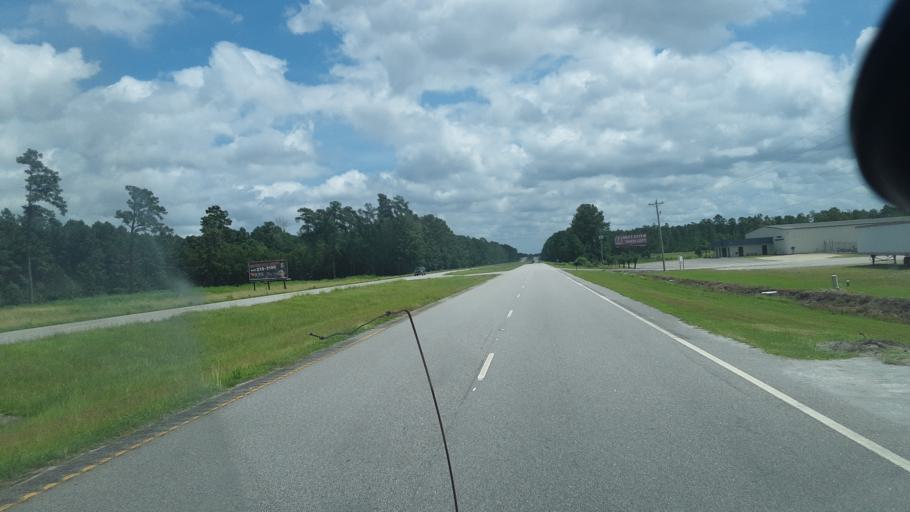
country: US
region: South Carolina
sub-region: Horry County
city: Loris
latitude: 34.0882
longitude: -78.8921
